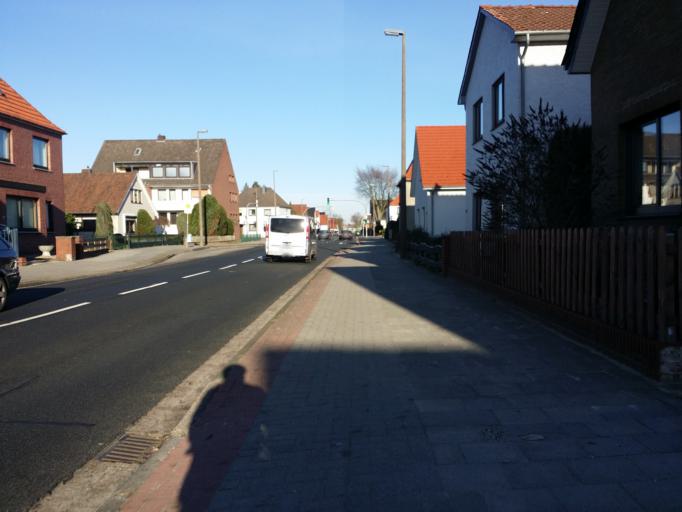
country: DE
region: Lower Saxony
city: Delmenhorst
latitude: 53.0449
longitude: 8.6556
